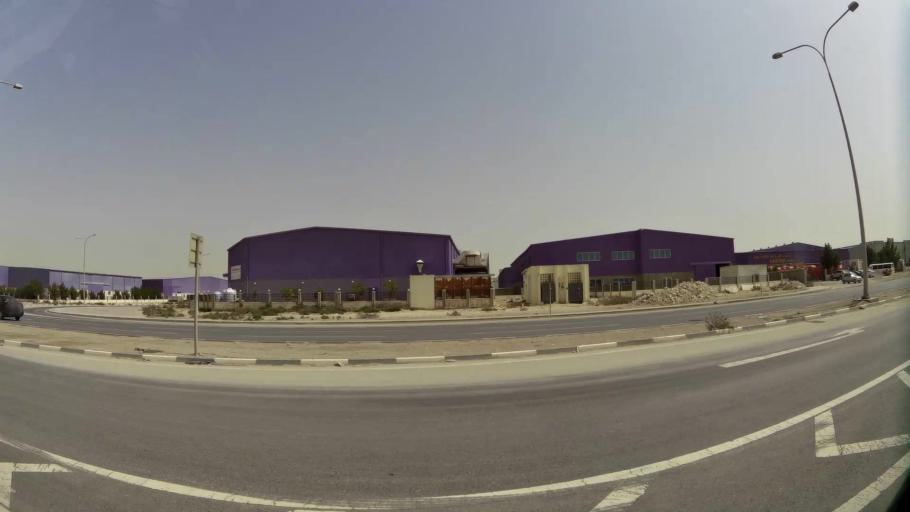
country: QA
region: Baladiyat ar Rayyan
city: Ar Rayyan
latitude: 25.1620
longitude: 51.4064
